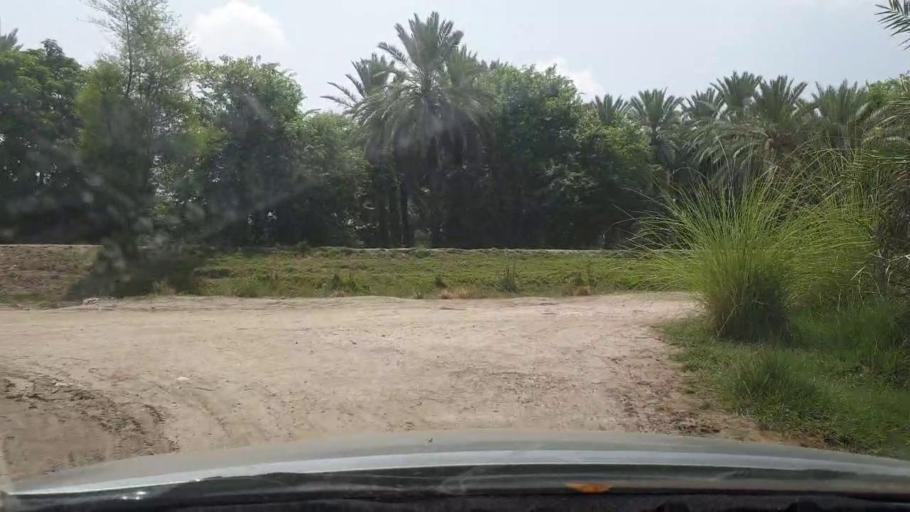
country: PK
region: Sindh
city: Khairpur
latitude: 27.4827
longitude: 68.7342
